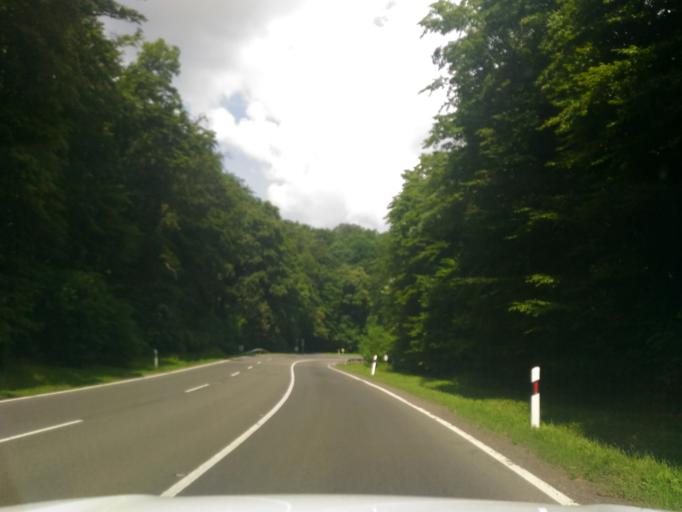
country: HU
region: Baranya
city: Komlo
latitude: 46.1409
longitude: 18.2502
